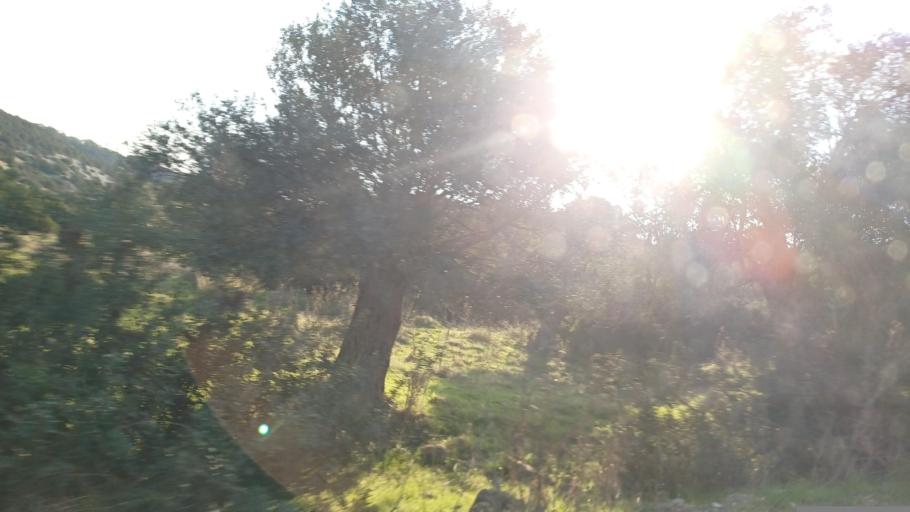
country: CY
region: Pafos
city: Pegeia
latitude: 34.9075
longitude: 32.3337
